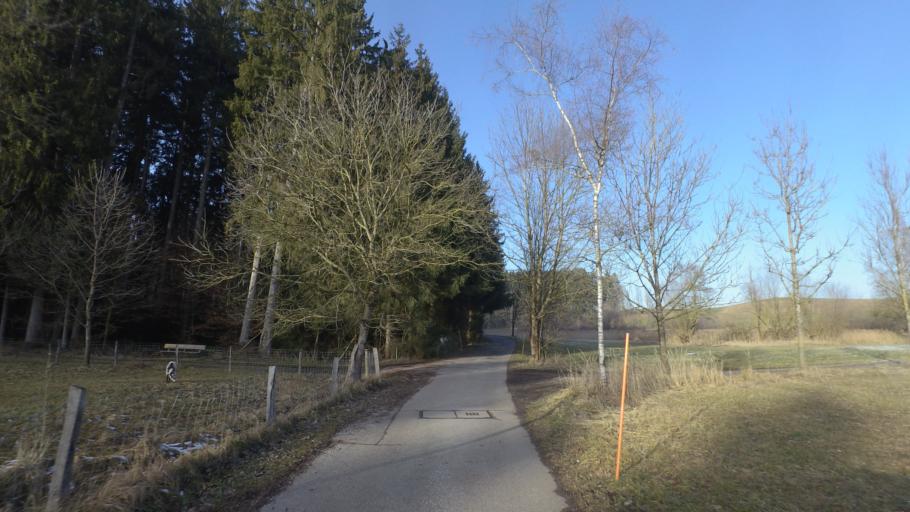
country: DE
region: Bavaria
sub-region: Upper Bavaria
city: Nussdorf
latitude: 47.9166
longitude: 12.5875
